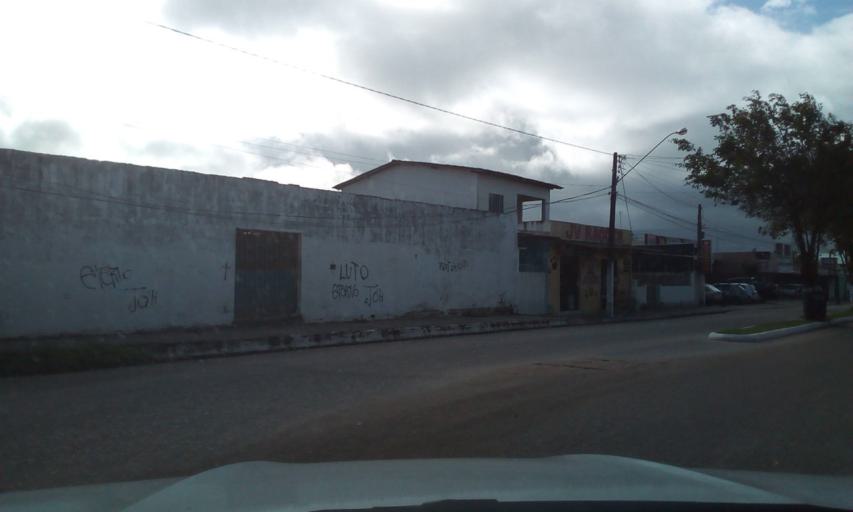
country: BR
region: Paraiba
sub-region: Conde
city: Conde
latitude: -7.2124
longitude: -34.8505
